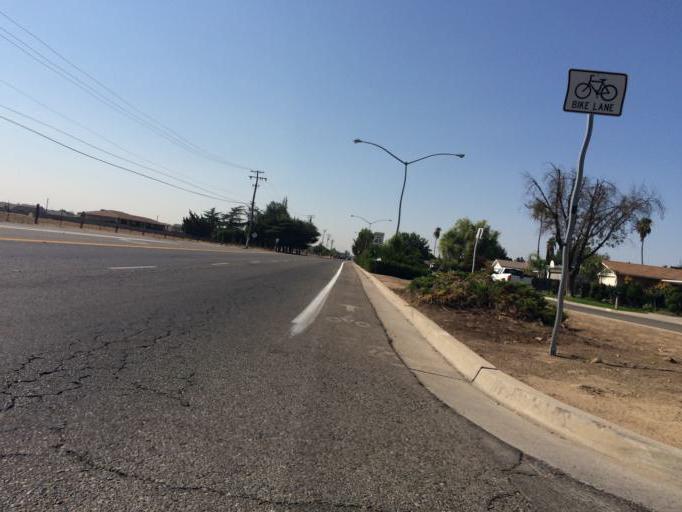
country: US
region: California
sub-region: Fresno County
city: Tarpey Village
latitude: 36.7867
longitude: -119.6823
